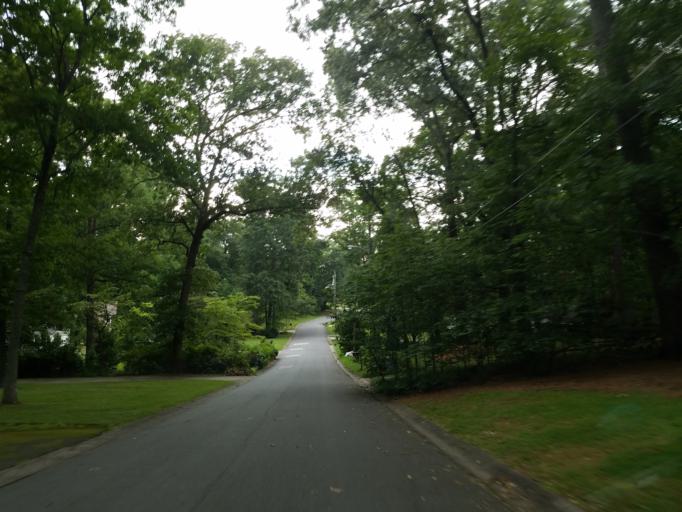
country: US
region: Georgia
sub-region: Cobb County
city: Marietta
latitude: 33.9389
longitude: -84.5508
